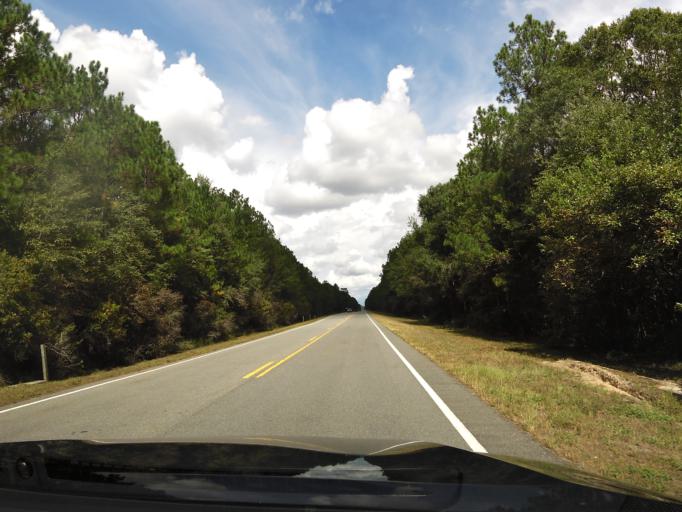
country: US
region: Georgia
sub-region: Charlton County
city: Folkston
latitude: 31.0185
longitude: -82.0245
